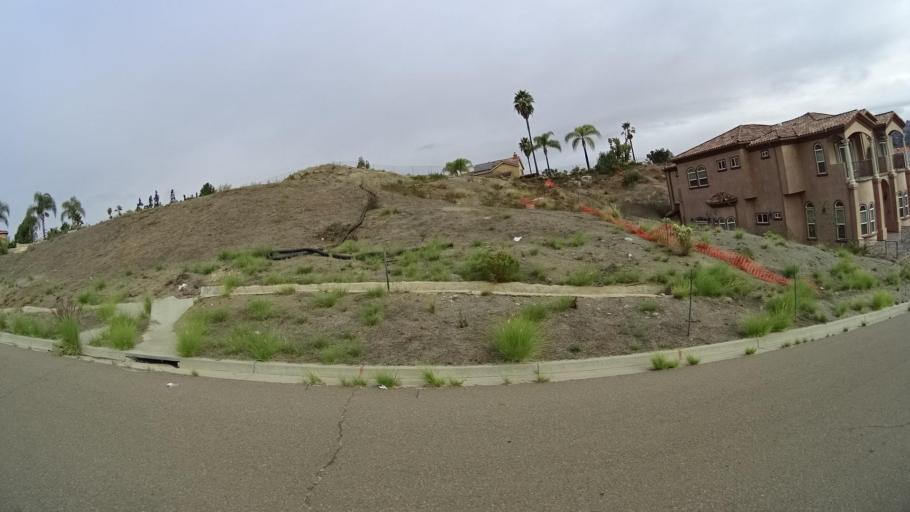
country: US
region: California
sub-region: San Diego County
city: Rancho San Diego
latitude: 32.7627
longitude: -116.9306
